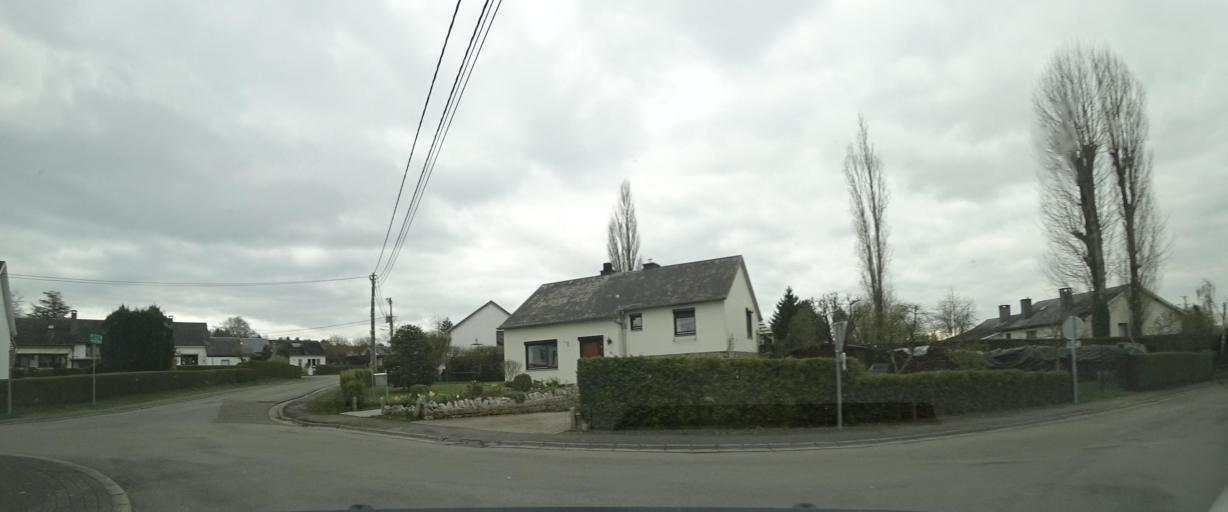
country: BE
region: Wallonia
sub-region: Province du Luxembourg
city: Marche-en-Famenne
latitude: 50.2234
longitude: 5.3500
